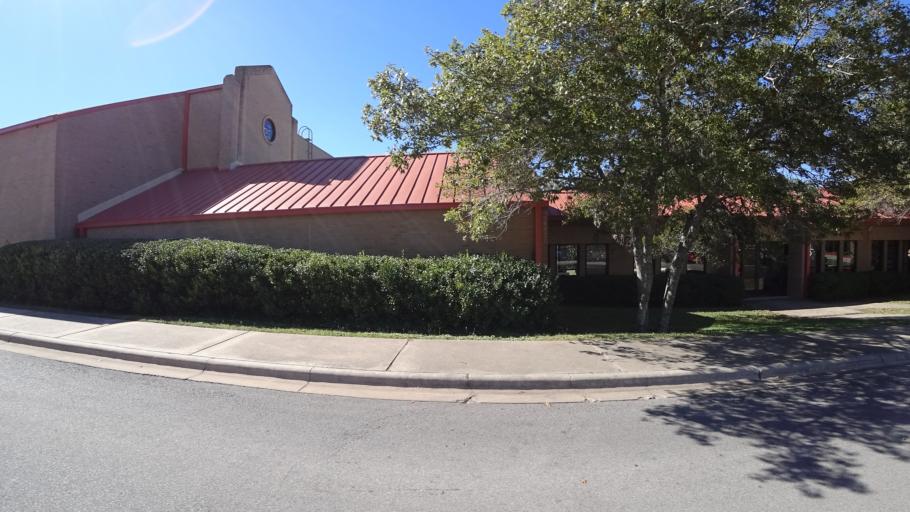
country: US
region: Texas
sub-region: Travis County
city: Austin
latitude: 30.2302
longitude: -97.7576
